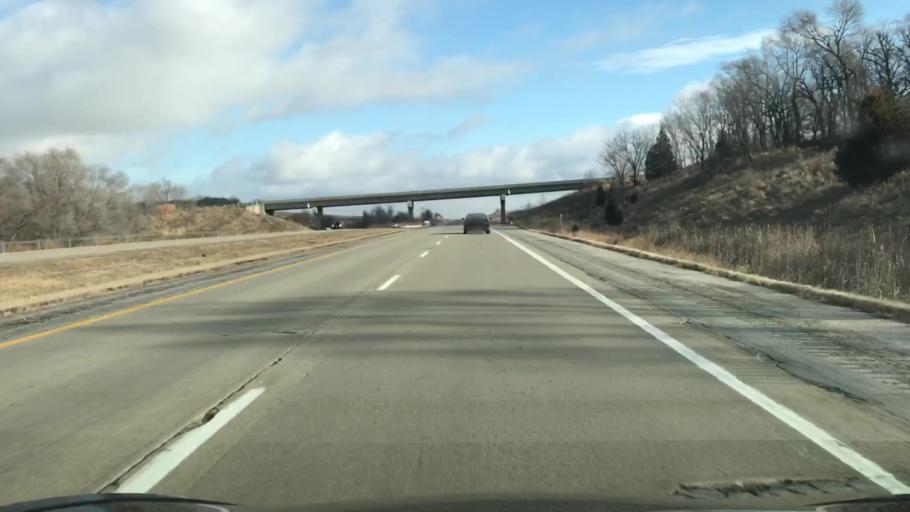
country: US
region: Iowa
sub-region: Cass County
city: Atlantic
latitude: 41.4970
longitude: -94.8370
